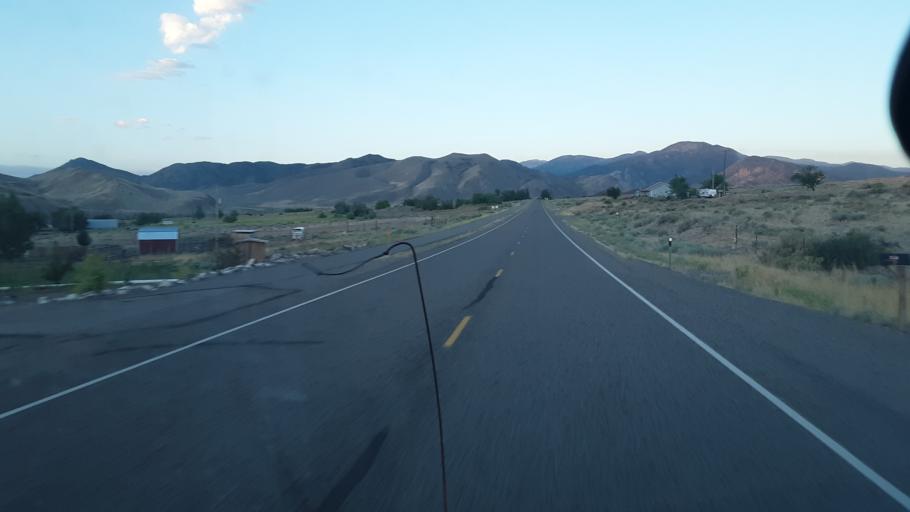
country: US
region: Utah
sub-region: Sevier County
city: Monroe
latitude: 38.6116
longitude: -112.2237
